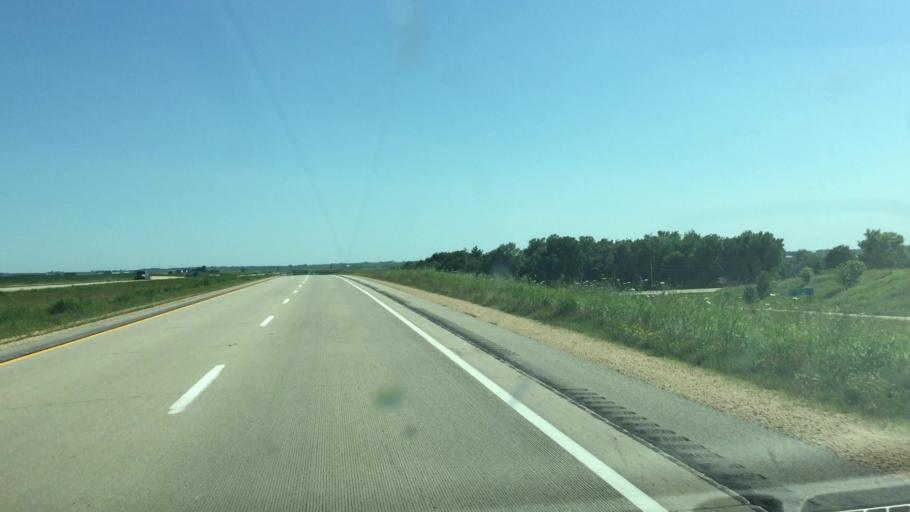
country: US
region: Iowa
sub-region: Jones County
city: Monticello
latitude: 42.2329
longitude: -91.1708
